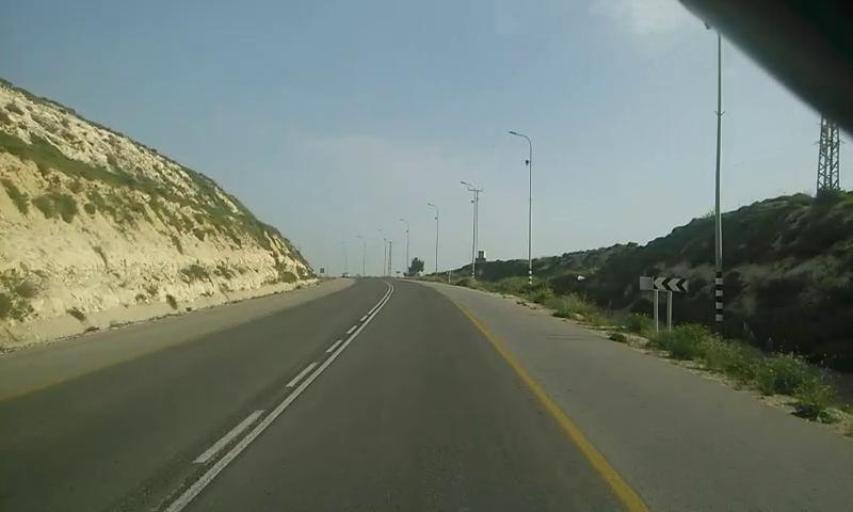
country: PS
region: West Bank
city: Sarrah
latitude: 32.1967
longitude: 35.1859
